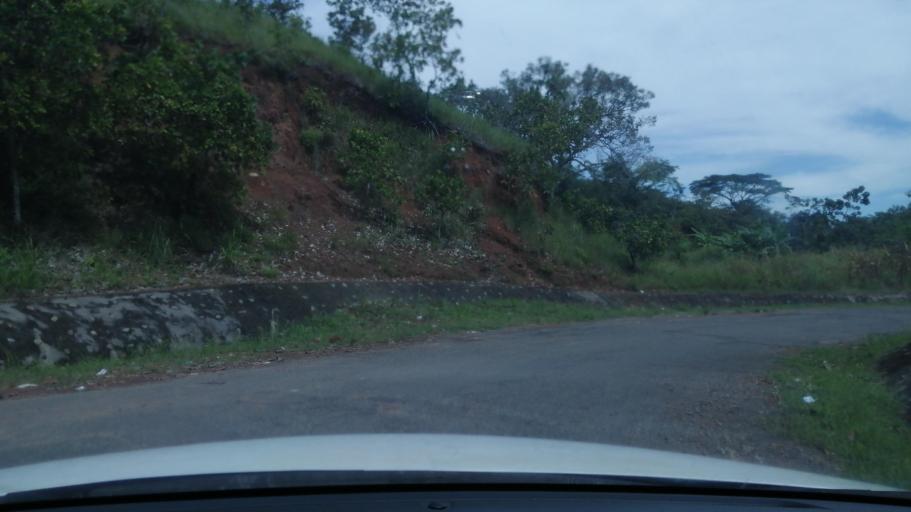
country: PA
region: Chiriqui
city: David
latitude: 8.4071
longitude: -82.4402
